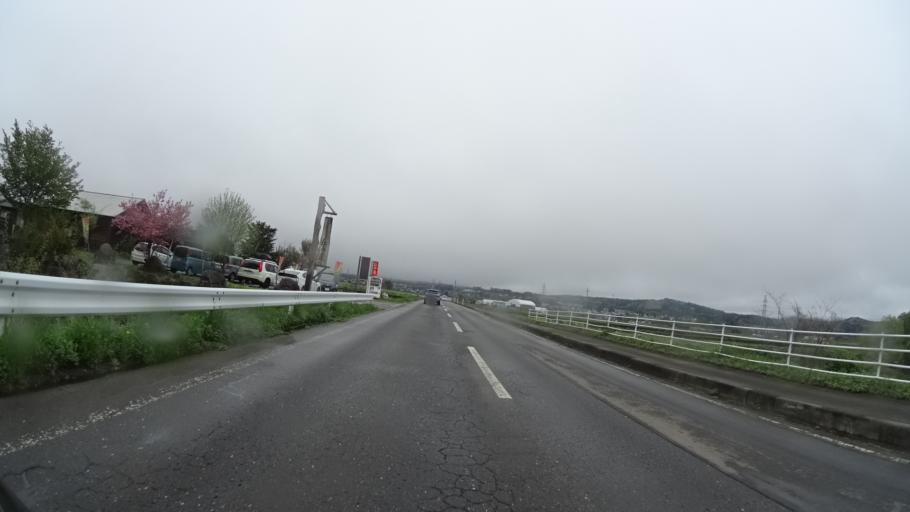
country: JP
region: Nagano
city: Nagano-shi
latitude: 36.7947
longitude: 138.1955
